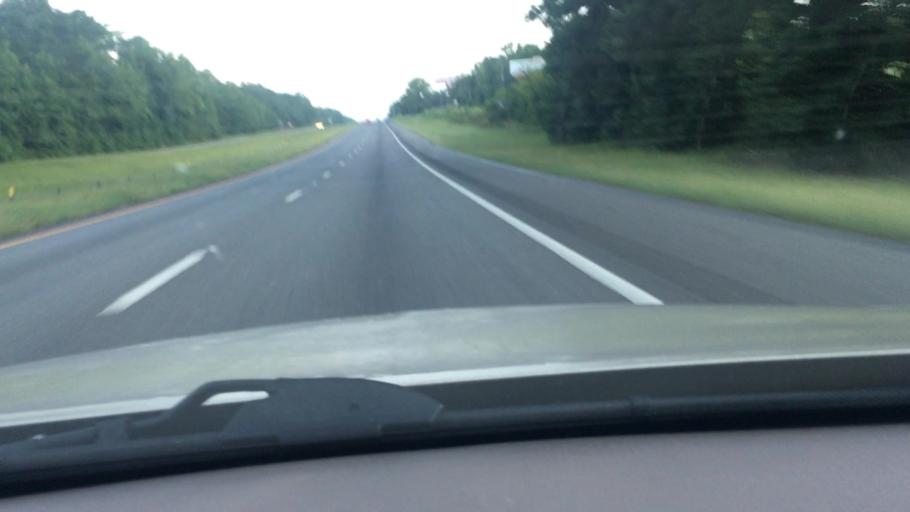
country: US
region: South Carolina
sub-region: Lexington County
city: Irmo
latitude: 34.1119
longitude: -81.1879
